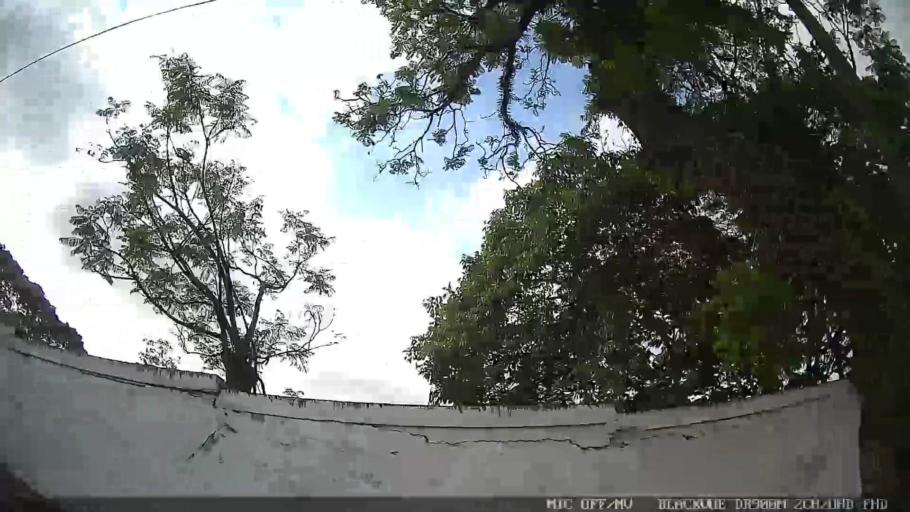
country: BR
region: Sao Paulo
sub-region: Sao Caetano Do Sul
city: Sao Caetano do Sul
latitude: -23.5702
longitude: -46.5295
